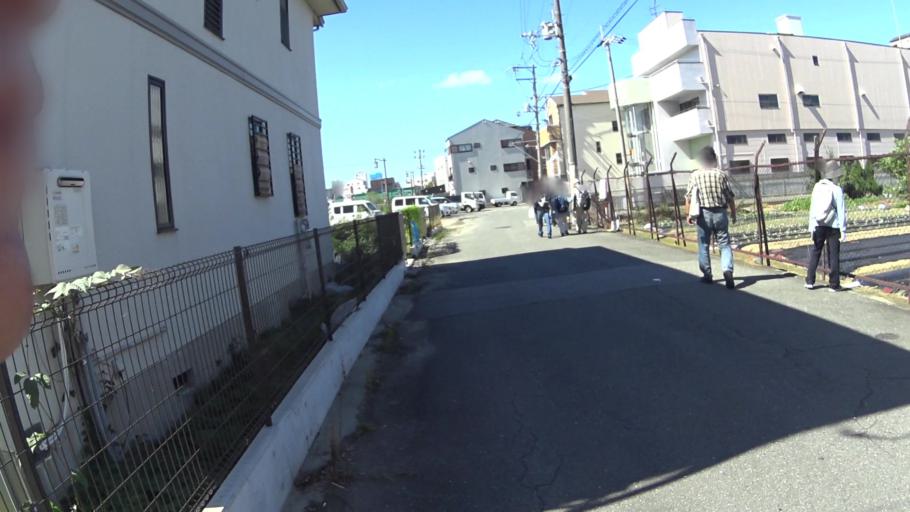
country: JP
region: Osaka
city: Yao
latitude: 34.6335
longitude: 135.5542
